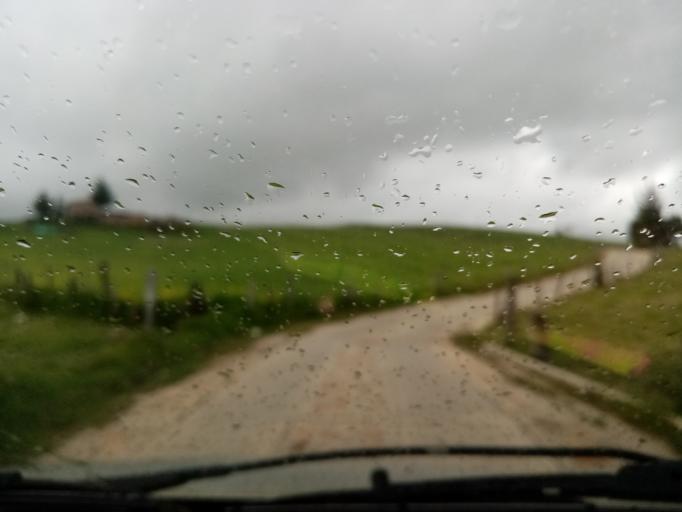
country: CO
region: Boyaca
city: Siachoque
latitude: 5.5551
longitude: -73.2512
